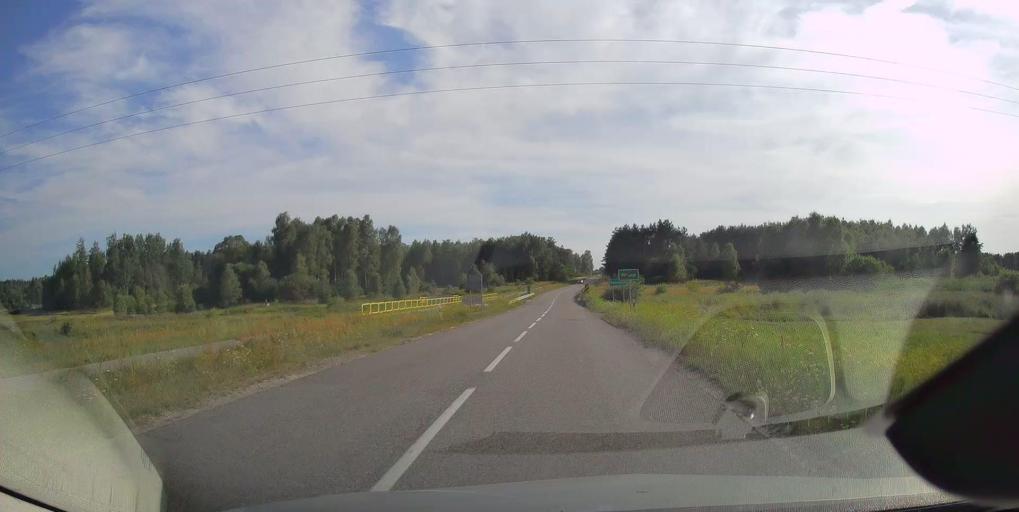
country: PL
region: Swietokrzyskie
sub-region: Powiat konecki
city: Radoszyce
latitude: 51.0813
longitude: 20.2850
